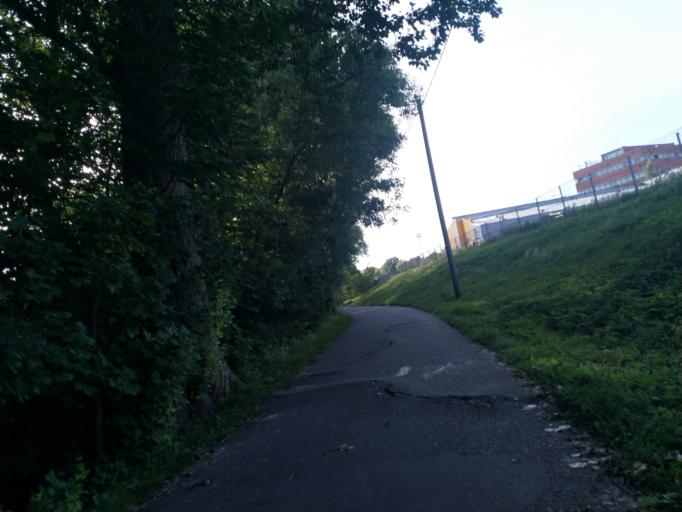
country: EE
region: Paernumaa
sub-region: Paernu linn
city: Parnu
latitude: 58.3872
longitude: 24.5291
